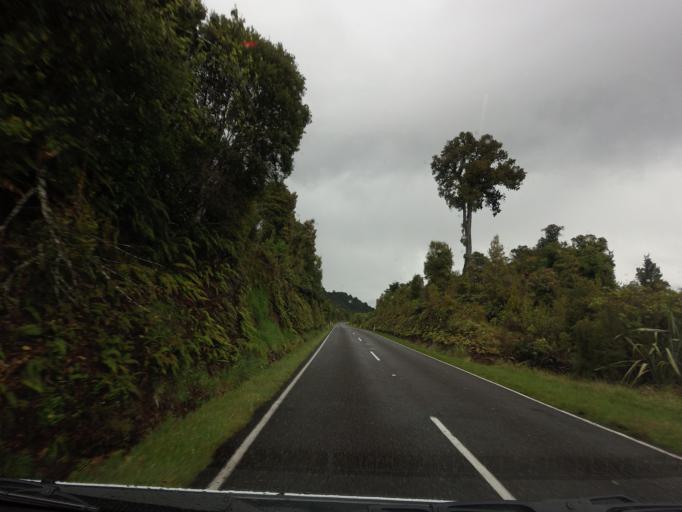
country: NZ
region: West Coast
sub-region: Westland District
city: Hokitika
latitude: -43.0547
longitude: 170.6368
